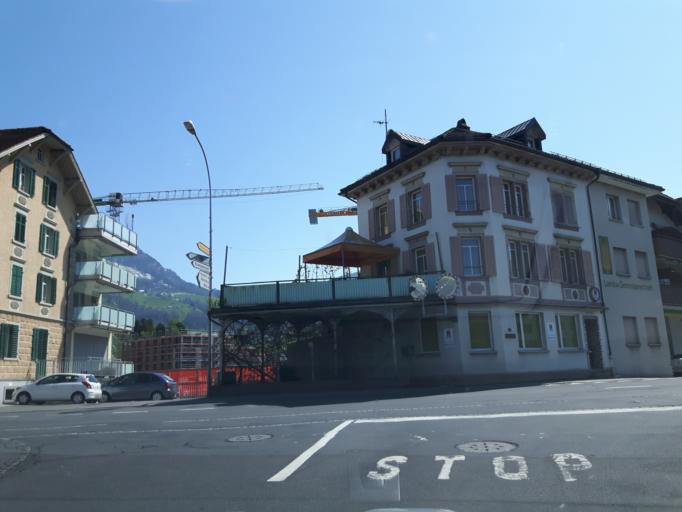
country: CH
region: Schwyz
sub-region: Bezirk Schwyz
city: Ibach
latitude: 47.0114
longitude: 8.6444
